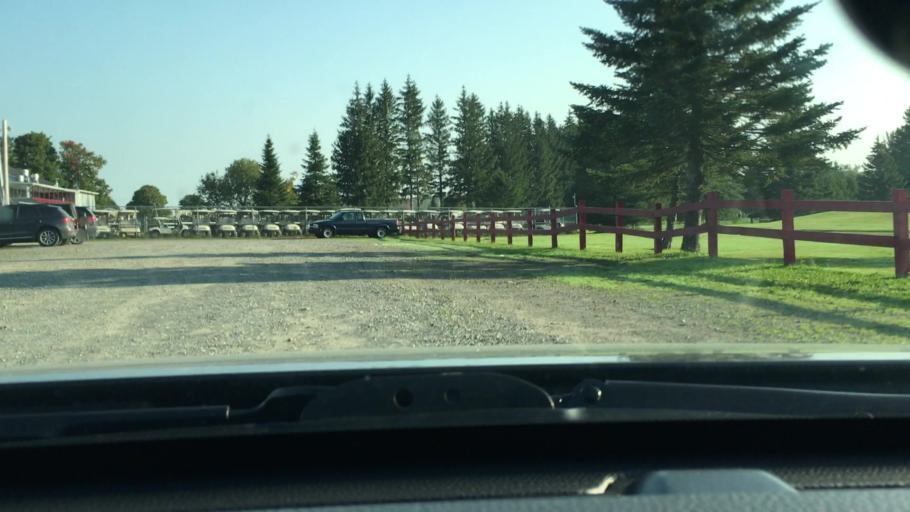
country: CA
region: Quebec
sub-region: Monteregie
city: Waterloo
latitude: 45.3561
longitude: -72.4891
